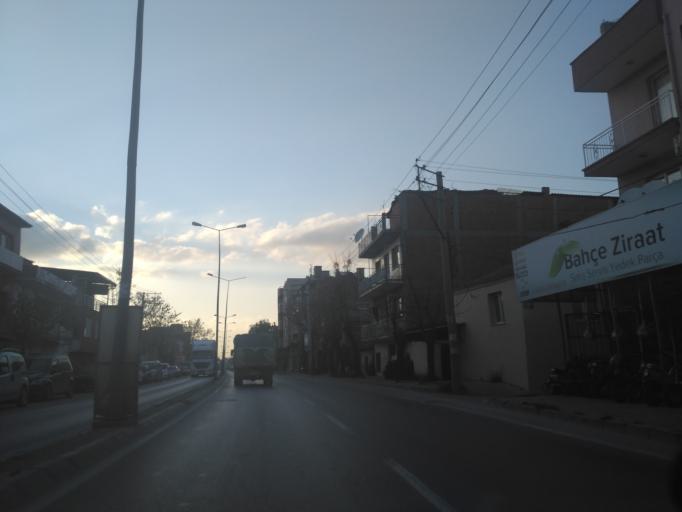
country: TR
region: Izmir
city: Buca
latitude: 38.4330
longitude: 27.1875
